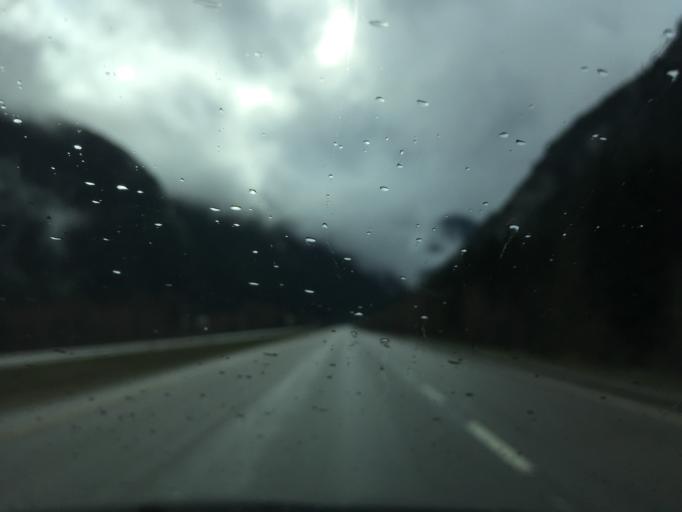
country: CA
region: British Columbia
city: Hope
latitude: 49.4505
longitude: -121.2652
